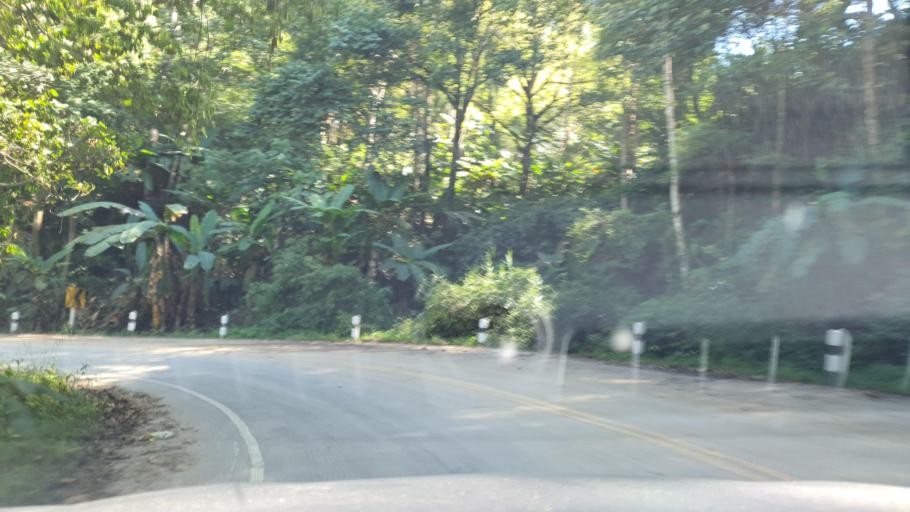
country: TH
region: Chiang Mai
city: Phrao
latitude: 19.3108
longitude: 99.3328
